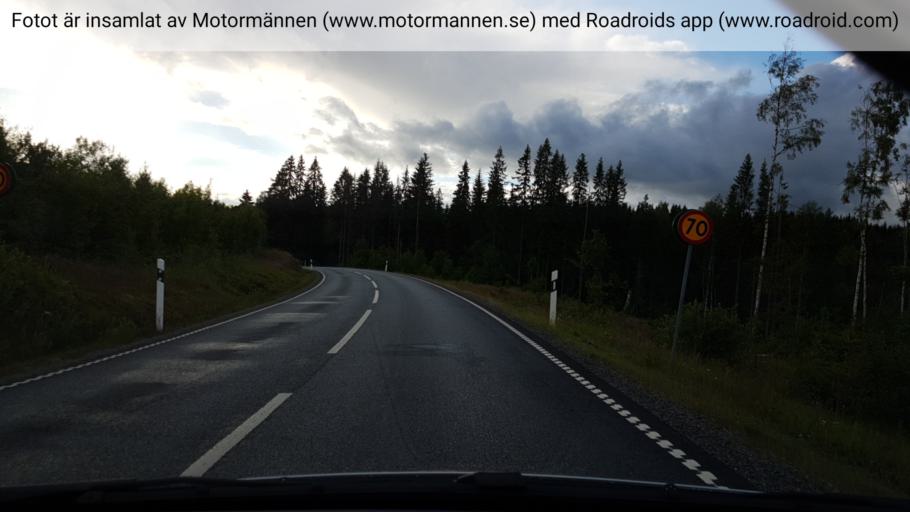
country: SE
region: OErebro
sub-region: Hallefors Kommun
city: Haellefors
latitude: 59.8155
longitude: 14.6605
